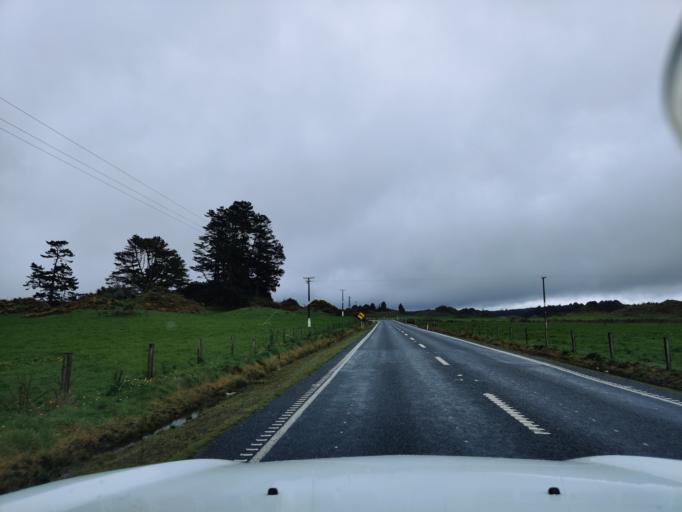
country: NZ
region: Bay of Plenty
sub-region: Rotorua District
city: Rotorua
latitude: -38.0465
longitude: 176.0701
